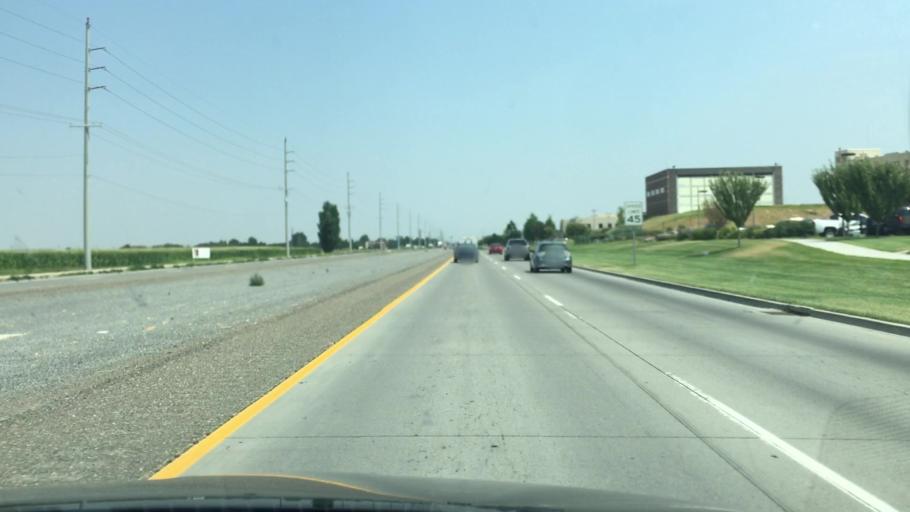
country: US
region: Idaho
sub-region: Twin Falls County
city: Twin Falls
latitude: 42.5916
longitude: -114.4978
